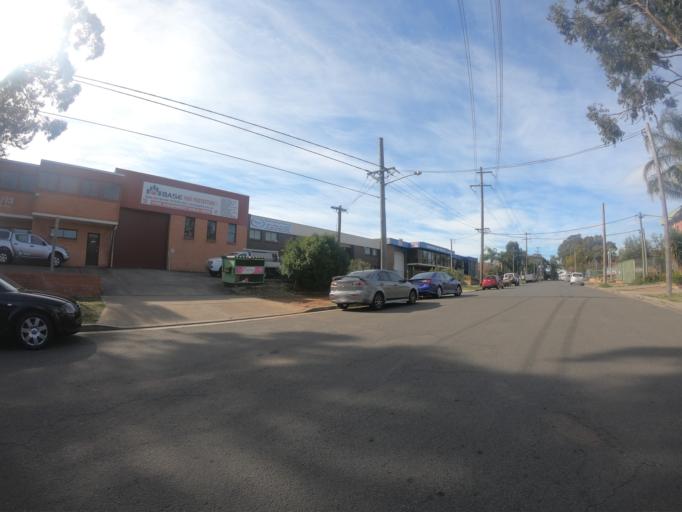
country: AU
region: New South Wales
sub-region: Bankstown
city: Padstow
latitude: -33.9454
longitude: 151.0354
